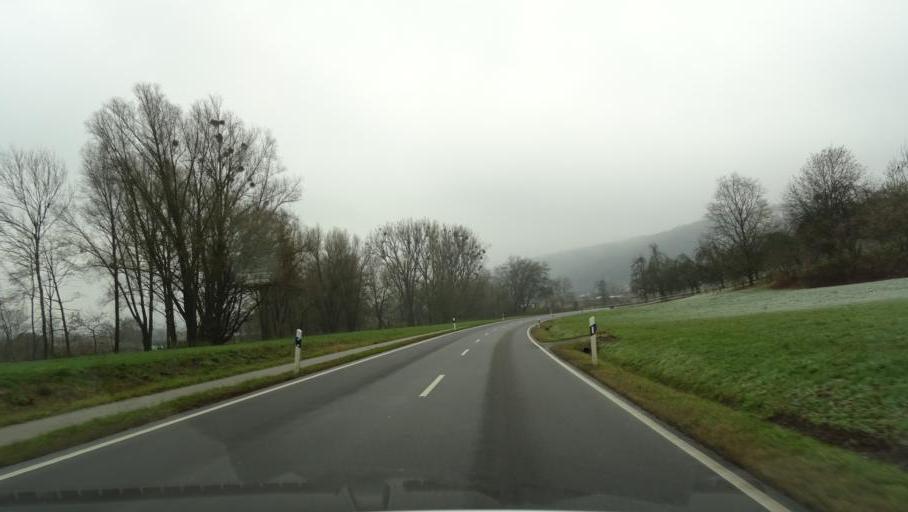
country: DE
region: Baden-Wuerttemberg
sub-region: Karlsruhe Region
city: Hassmersheim
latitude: 49.2883
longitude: 9.1316
